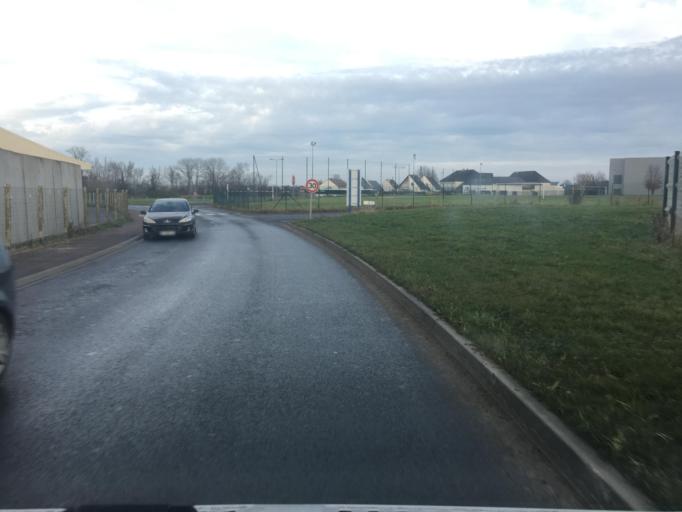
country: FR
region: Lower Normandy
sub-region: Departement du Calvados
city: Creully
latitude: 49.2767
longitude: -0.5454
